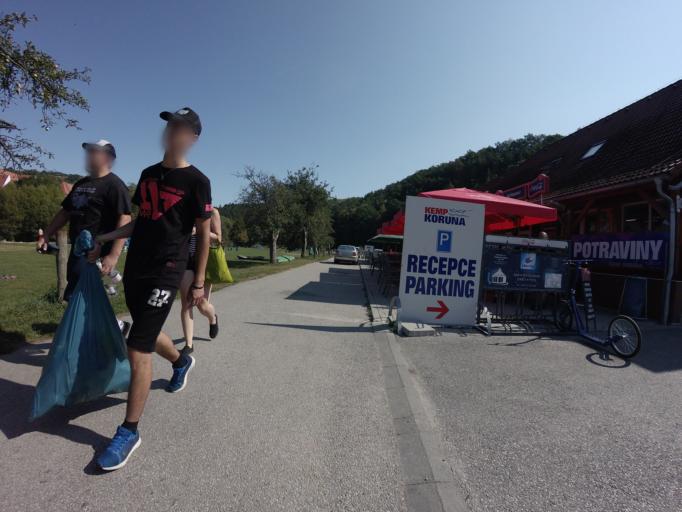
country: CZ
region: Jihocesky
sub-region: Okres Cesky Krumlov
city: Cesky Krumlov
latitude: 48.8532
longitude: 14.3716
